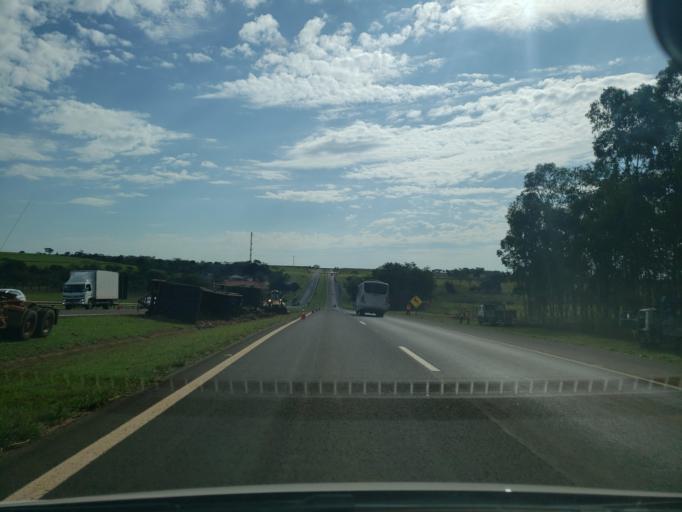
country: BR
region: Sao Paulo
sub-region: Promissao
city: Promissao
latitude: -21.6039
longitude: -49.8792
